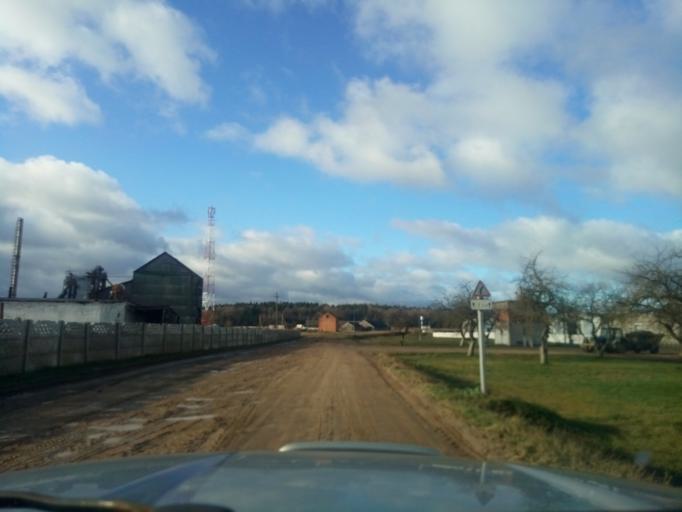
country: BY
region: Minsk
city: Tsimkavichy
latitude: 53.1801
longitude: 26.9543
